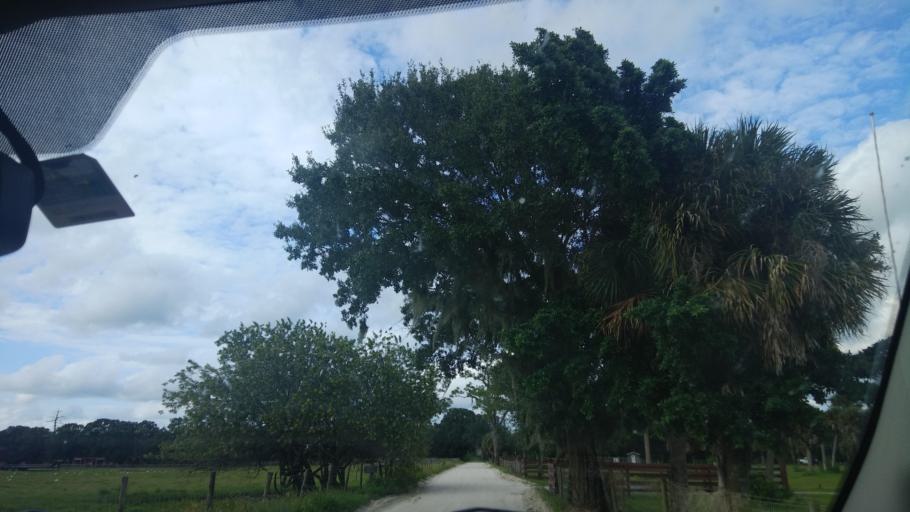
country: US
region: Florida
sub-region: Indian River County
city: Fellsmere
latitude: 27.7846
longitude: -80.5929
